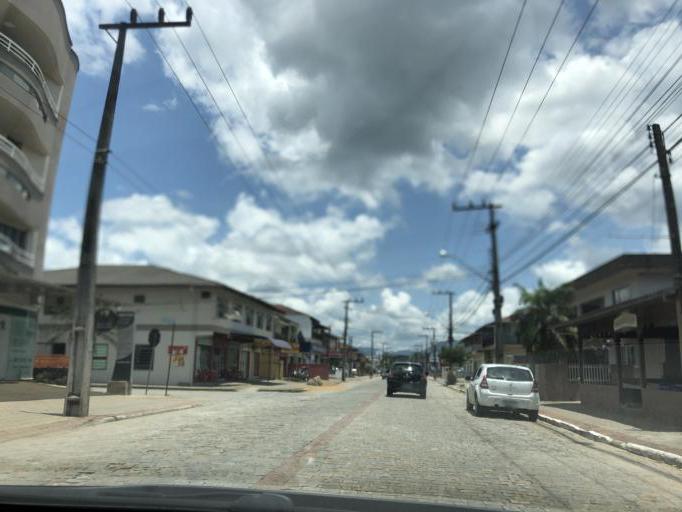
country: BR
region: Santa Catarina
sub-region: Jaragua Do Sul
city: Jaragua do Sul
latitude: -26.5170
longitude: -49.1312
